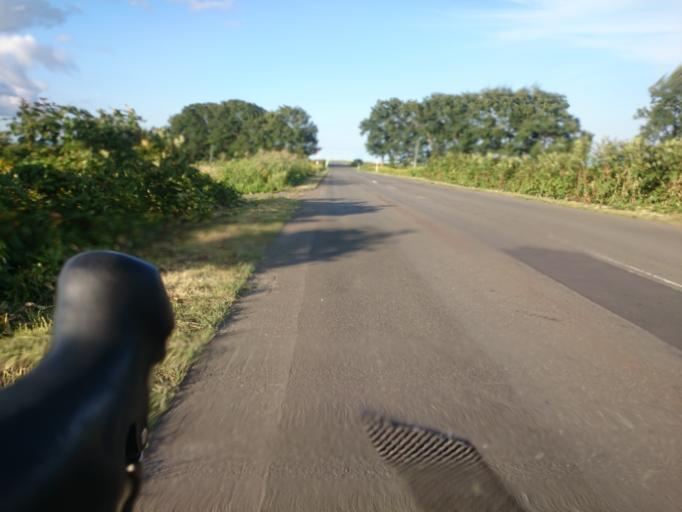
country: JP
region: Hokkaido
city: Tobetsu
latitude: 43.1842
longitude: 141.5592
